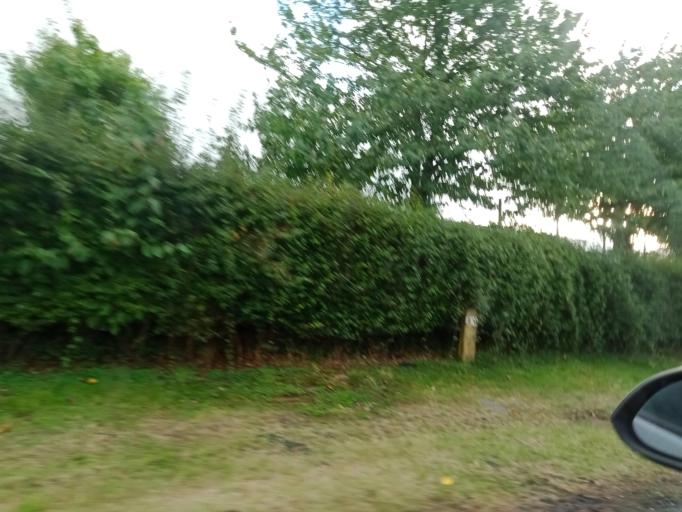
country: IE
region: Leinster
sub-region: Laois
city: Mountmellick
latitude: 53.1357
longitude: -7.4108
